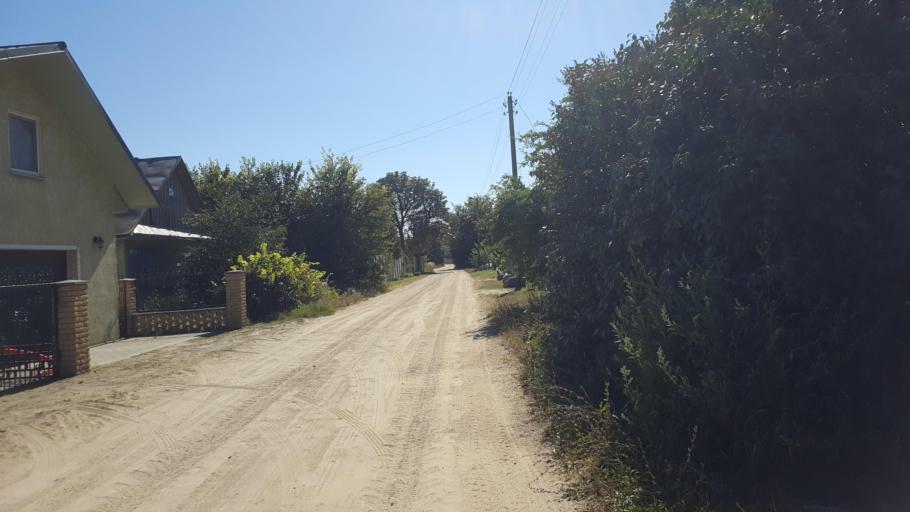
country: PL
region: Lublin Voivodeship
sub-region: Powiat bialski
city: Rokitno
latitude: 52.2216
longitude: 23.3428
